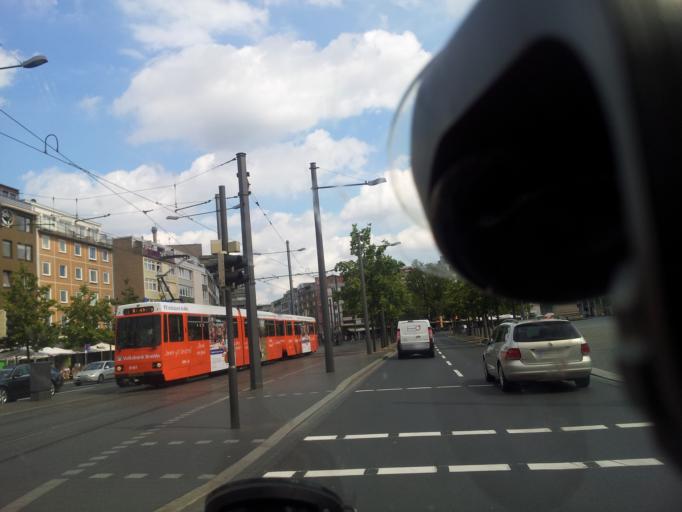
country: DE
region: Lower Saxony
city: Braunschweig
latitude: 52.2627
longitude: 10.5263
